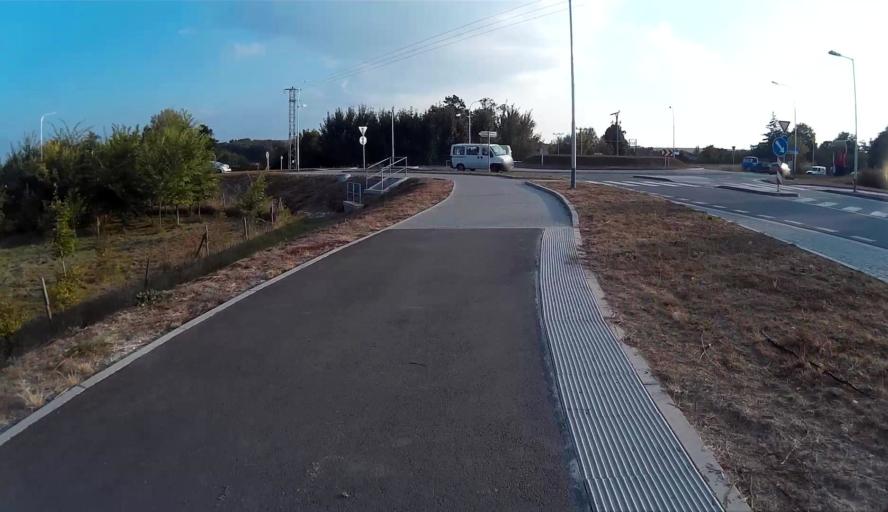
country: CZ
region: South Moravian
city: Podoli
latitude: 49.1834
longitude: 16.7227
